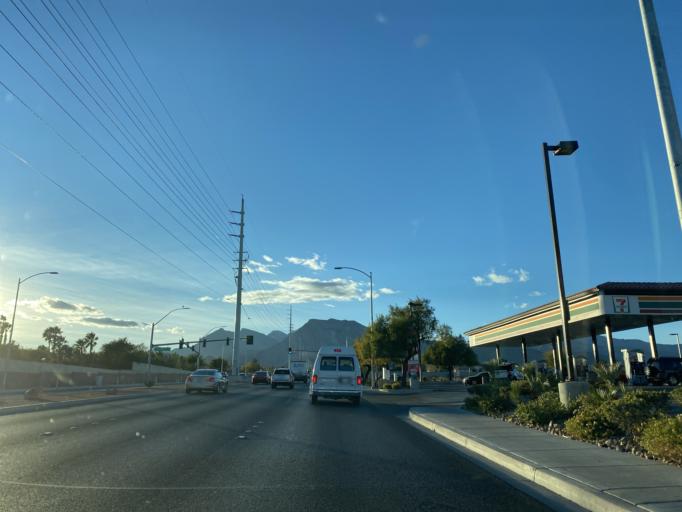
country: US
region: Nevada
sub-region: Clark County
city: Summerlin South
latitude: 36.2188
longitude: -115.2961
